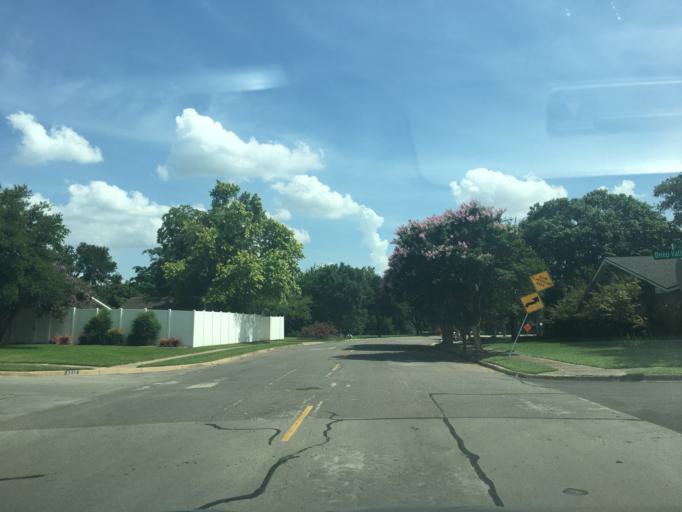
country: US
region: Texas
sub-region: Dallas County
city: Farmers Branch
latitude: 32.9125
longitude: -96.8460
